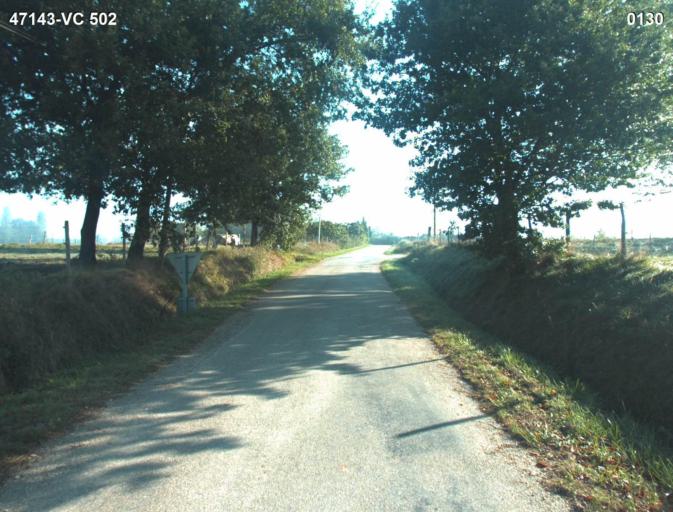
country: FR
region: Aquitaine
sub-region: Departement du Lot-et-Garonne
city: Lavardac
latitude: 44.1672
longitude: 0.3207
